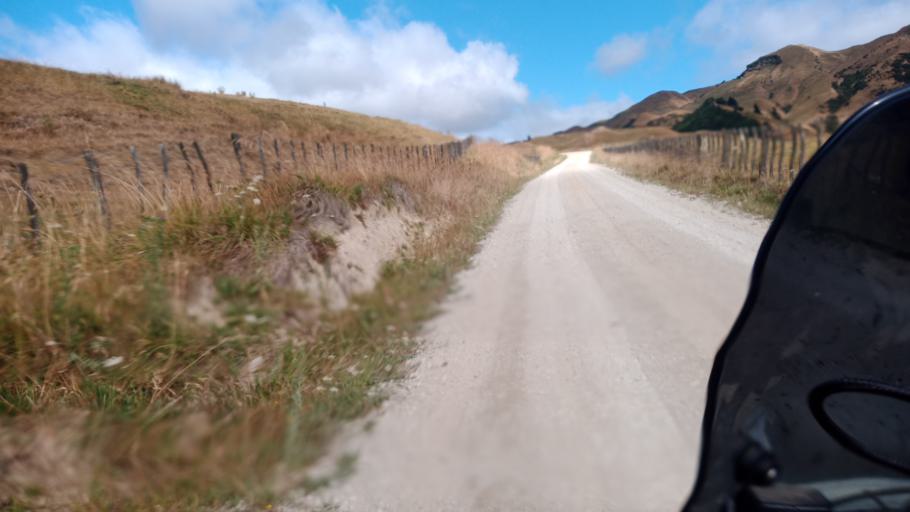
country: NZ
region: Hawke's Bay
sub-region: Wairoa District
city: Wairoa
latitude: -38.6021
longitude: 177.4835
